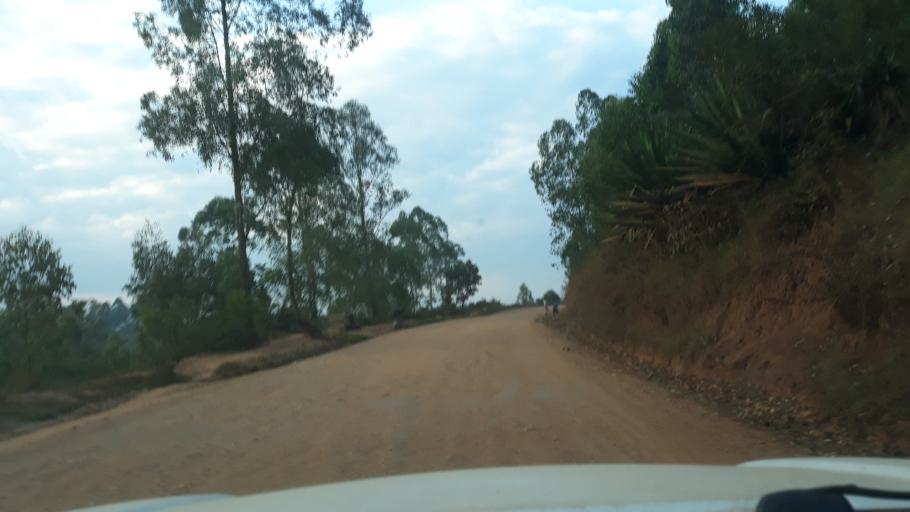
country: CD
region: South Kivu
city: Bukavu
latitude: -2.6263
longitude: 28.8741
